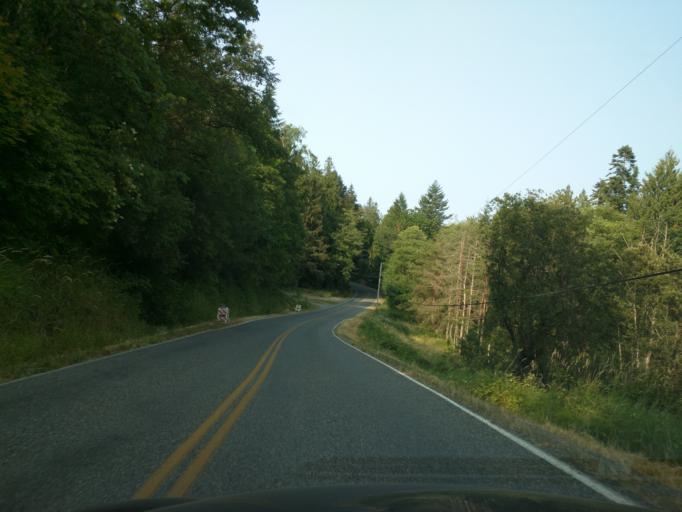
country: US
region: Washington
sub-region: Whatcom County
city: Sumas
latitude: 48.9337
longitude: -122.2509
